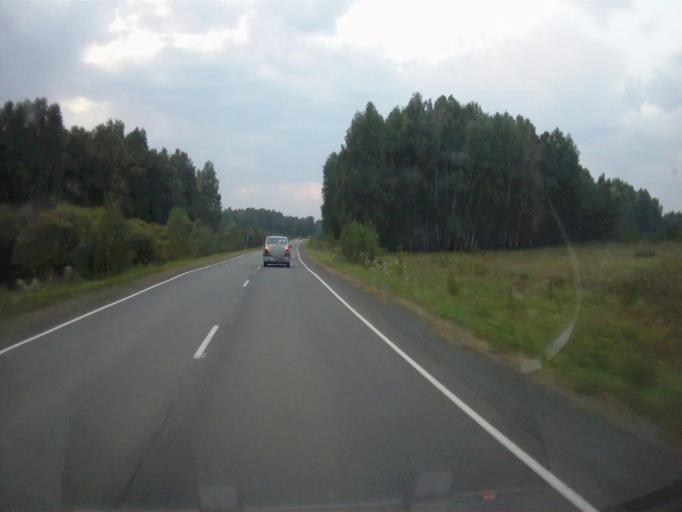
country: RU
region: Chelyabinsk
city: Chebarkul'
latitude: 55.1849
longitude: 60.4658
